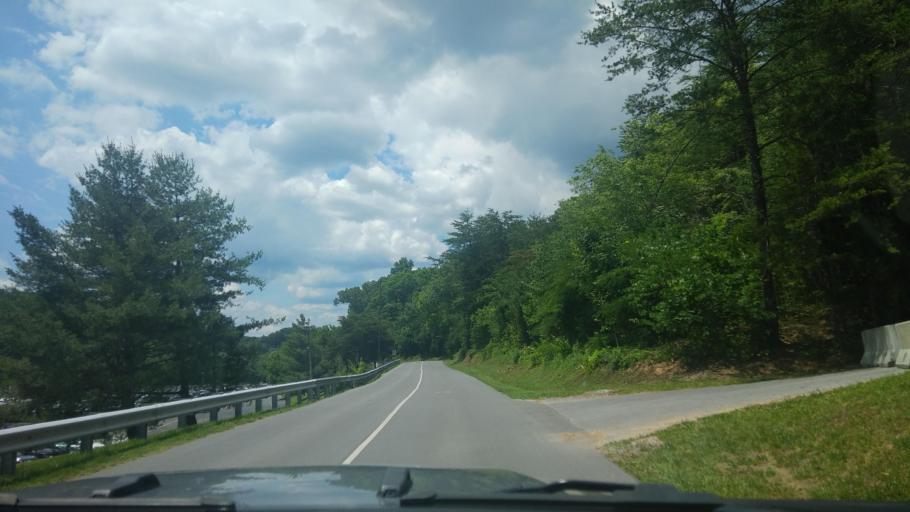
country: US
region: Tennessee
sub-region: Sevier County
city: Pigeon Forge
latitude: 35.8028
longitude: -83.5357
